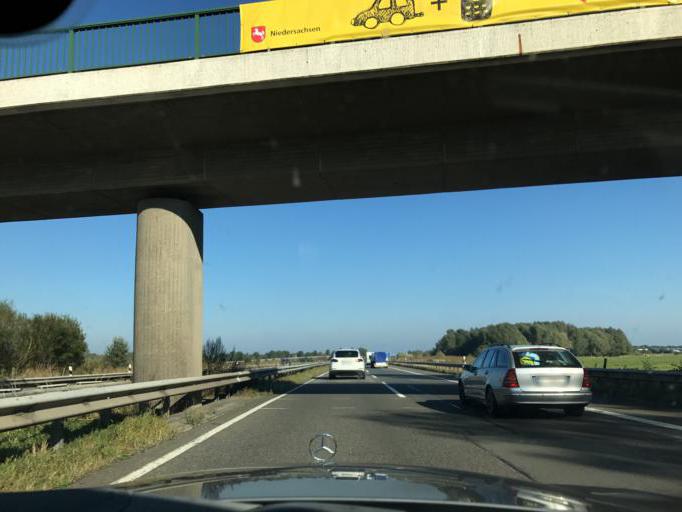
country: DE
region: Lower Saxony
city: Leer
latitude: 53.2558
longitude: 7.4382
